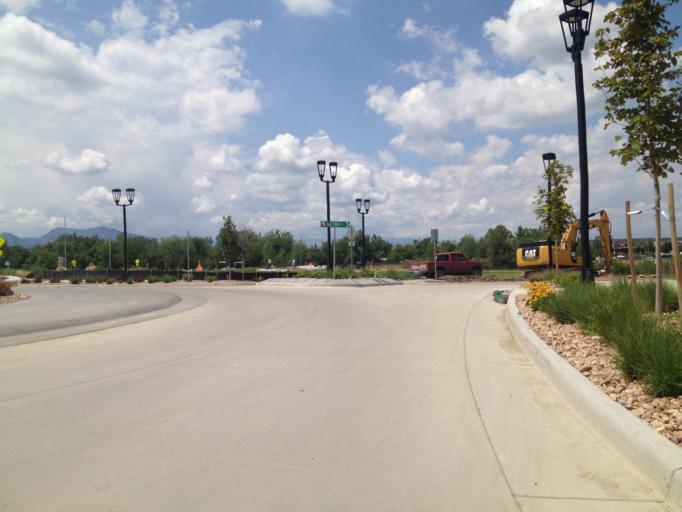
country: US
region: Colorado
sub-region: Boulder County
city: Superior
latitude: 39.9517
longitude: -105.1633
